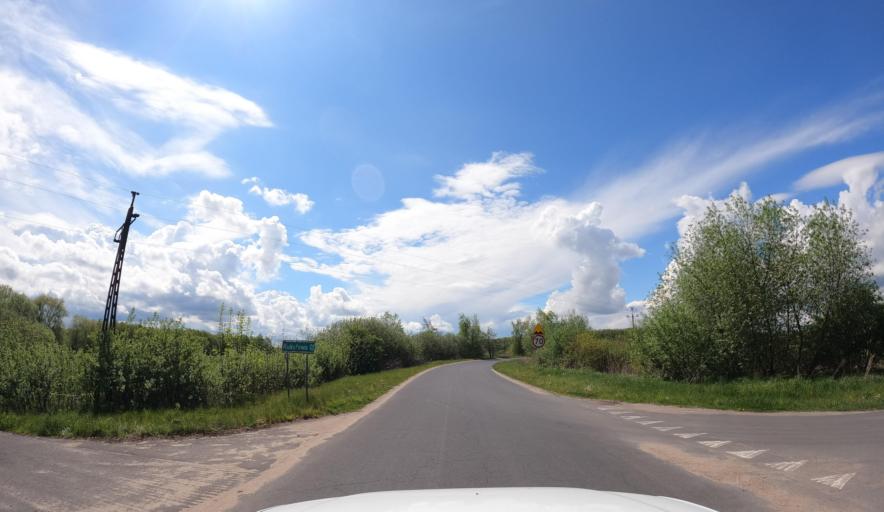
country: PL
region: West Pomeranian Voivodeship
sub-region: Powiat kamienski
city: Kamien Pomorski
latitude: 53.9165
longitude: 14.7033
